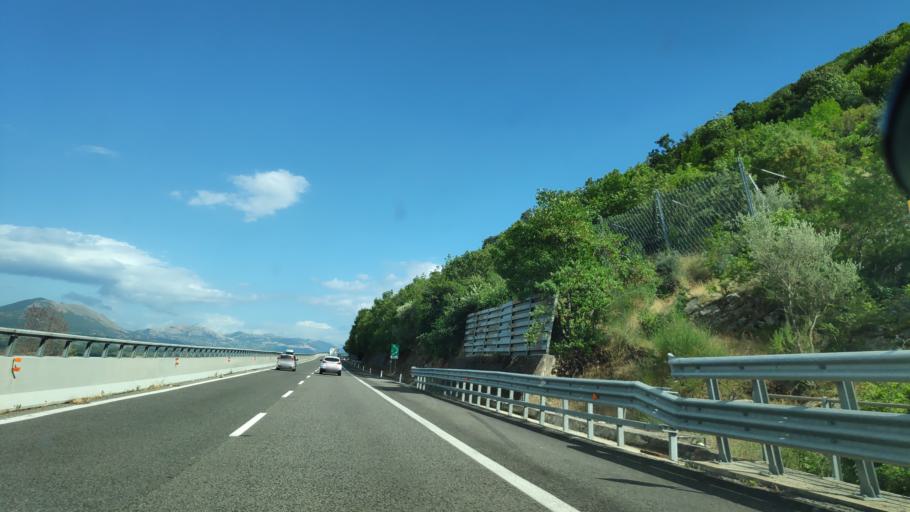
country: IT
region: Campania
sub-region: Provincia di Salerno
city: Sicignano degli Alburni
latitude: 40.5918
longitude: 15.3271
